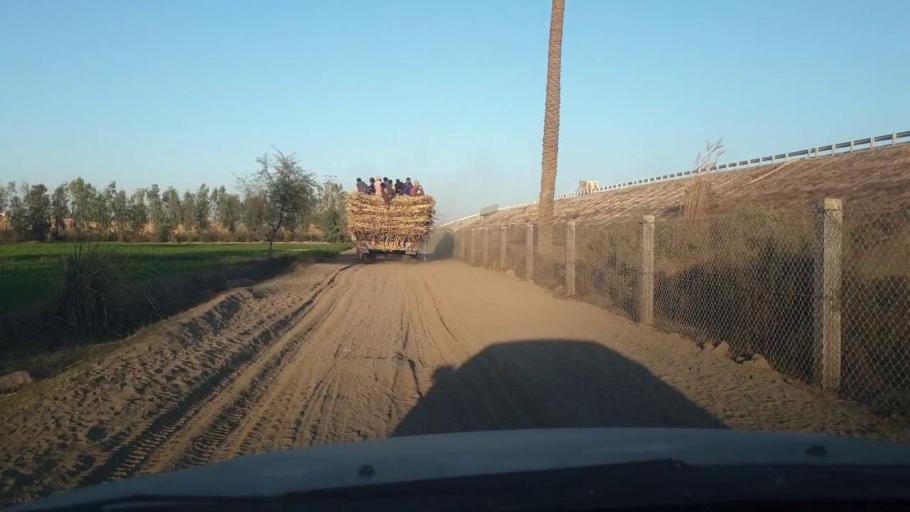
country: PK
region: Sindh
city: Ghotki
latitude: 28.0339
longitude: 69.3109
